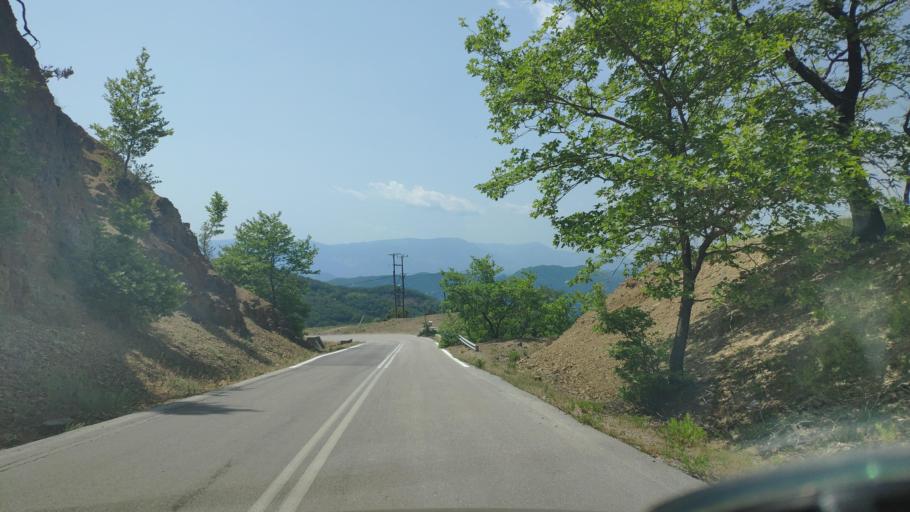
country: GR
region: Epirus
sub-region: Nomos Artas
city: Ano Kalentini
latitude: 39.2402
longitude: 21.2062
